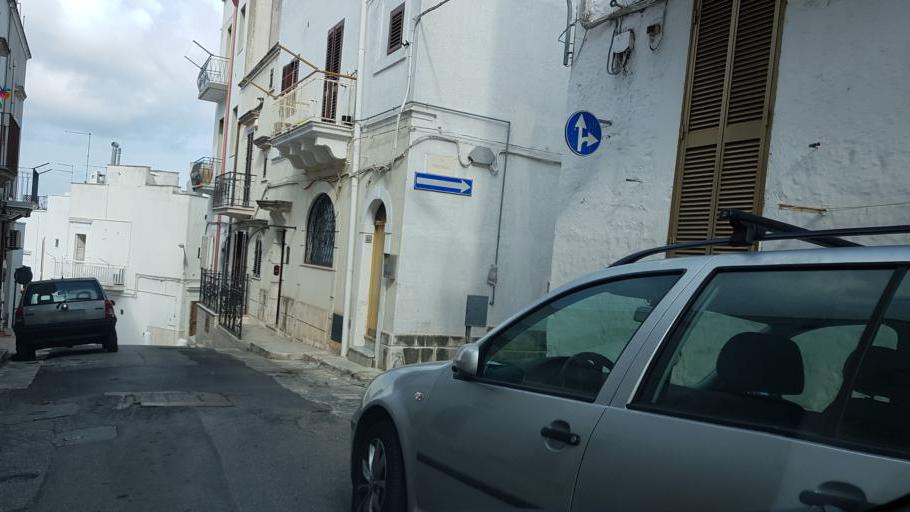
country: IT
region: Apulia
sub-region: Provincia di Brindisi
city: Ostuni
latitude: 40.7297
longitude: 17.5751
